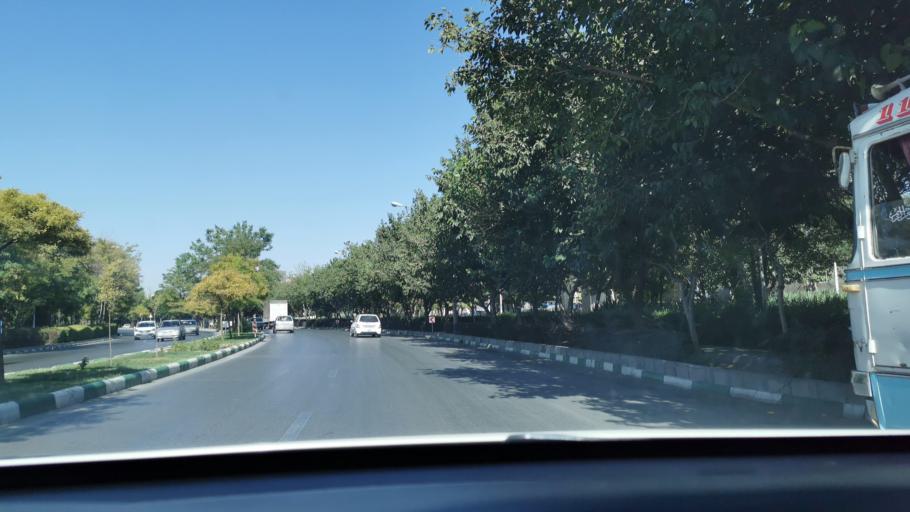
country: IR
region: Razavi Khorasan
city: Mashhad
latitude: 36.3353
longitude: 59.6338
